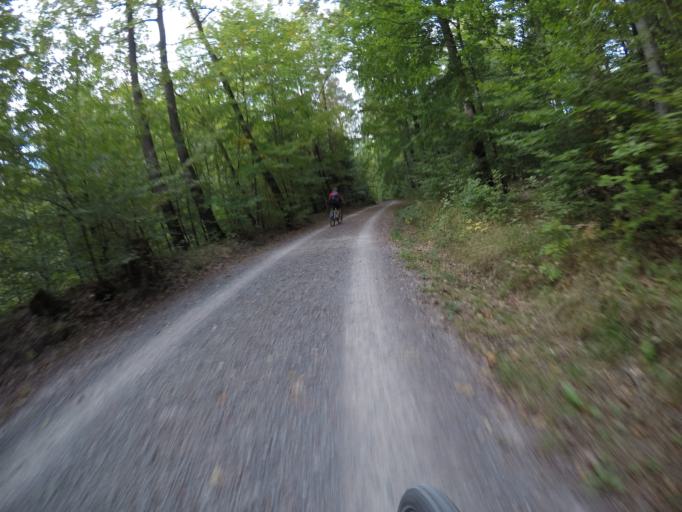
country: DE
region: Baden-Wuerttemberg
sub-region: Regierungsbezirk Stuttgart
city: Schonaich
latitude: 48.6709
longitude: 9.0494
